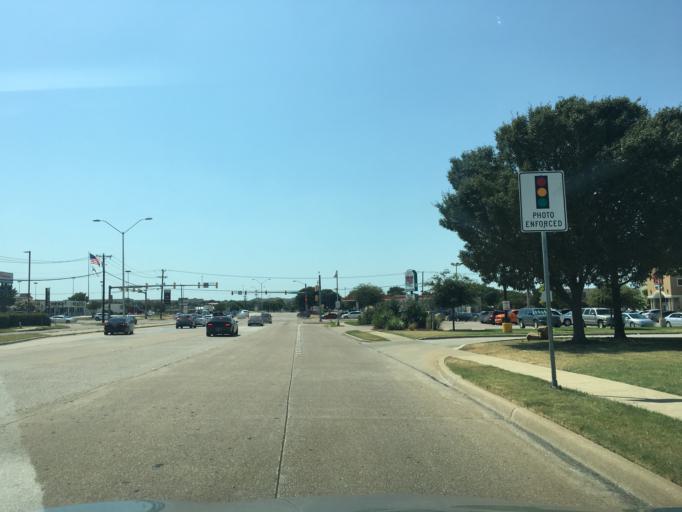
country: US
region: Texas
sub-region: Tarrant County
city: Edgecliff Village
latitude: 32.6351
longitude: -97.3683
